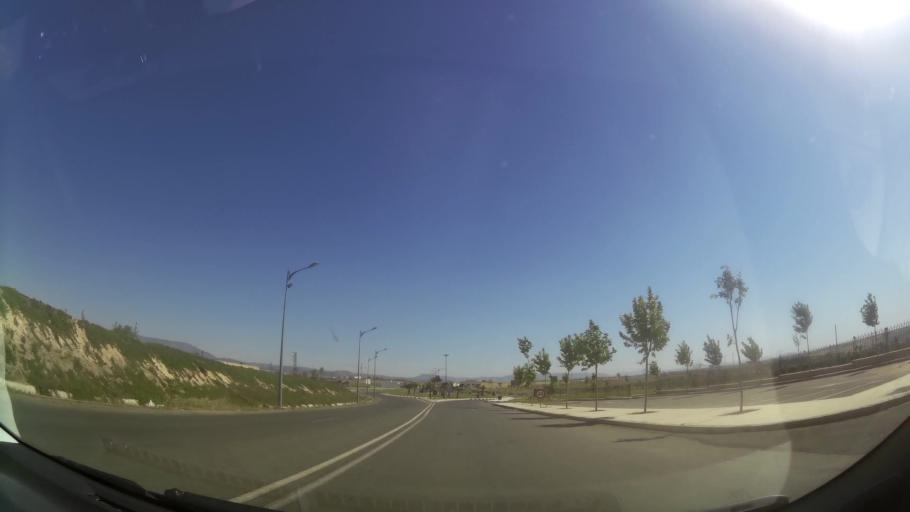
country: MA
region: Oriental
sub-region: Oujda-Angad
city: Oujda
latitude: 34.7384
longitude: -1.9188
